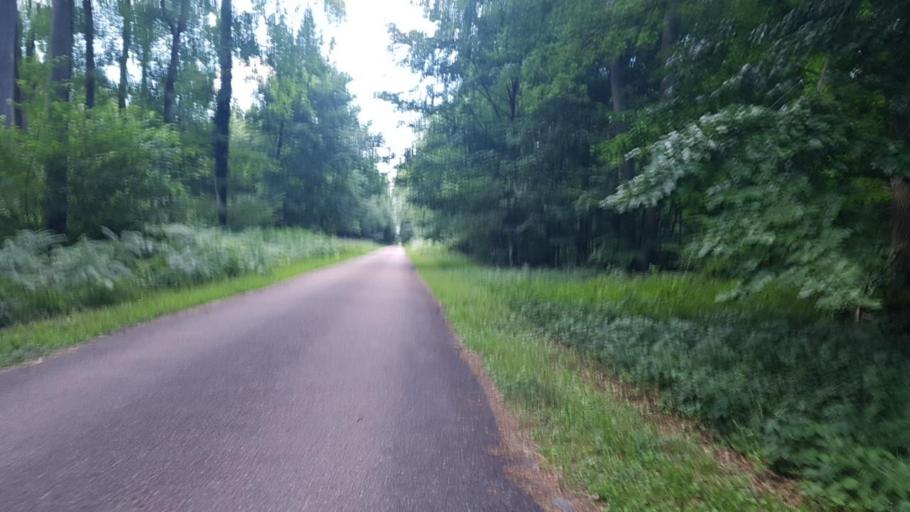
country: FR
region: Picardie
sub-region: Departement de l'Oise
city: Chamant
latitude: 49.1599
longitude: 2.6361
